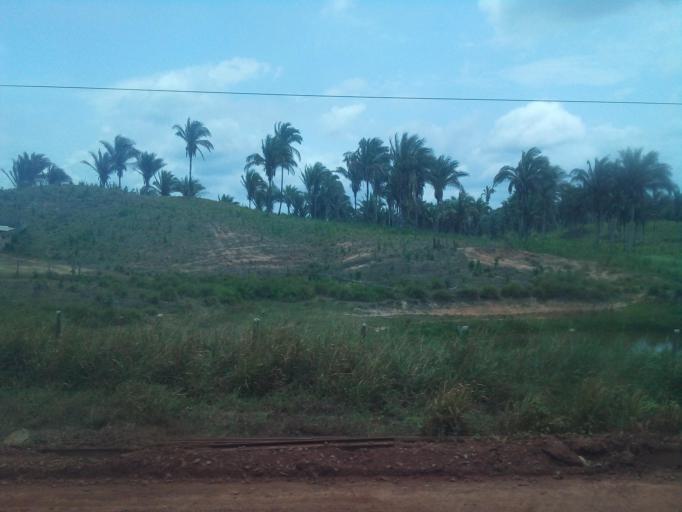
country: BR
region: Maranhao
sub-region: Santa Ines
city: Santa Ines
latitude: -3.6956
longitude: -45.6197
